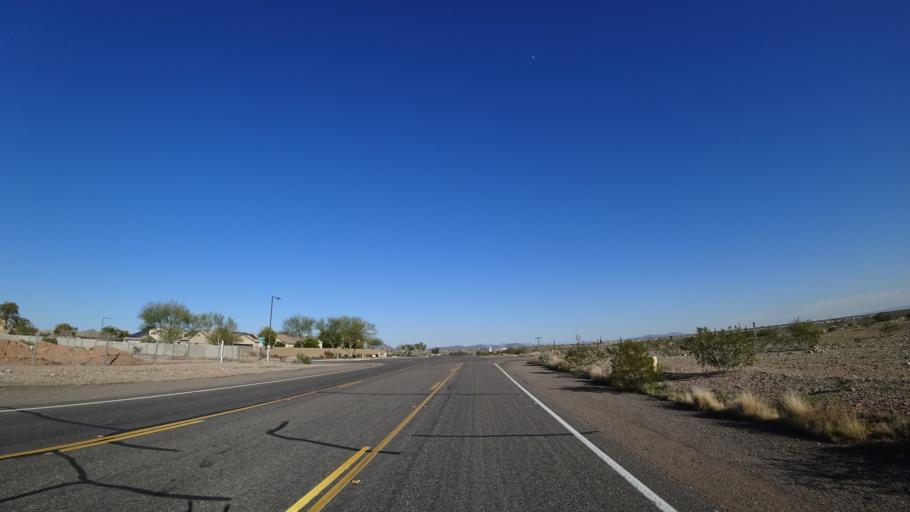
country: US
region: Arizona
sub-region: Maricopa County
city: Sun City West
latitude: 33.6893
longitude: -112.3216
